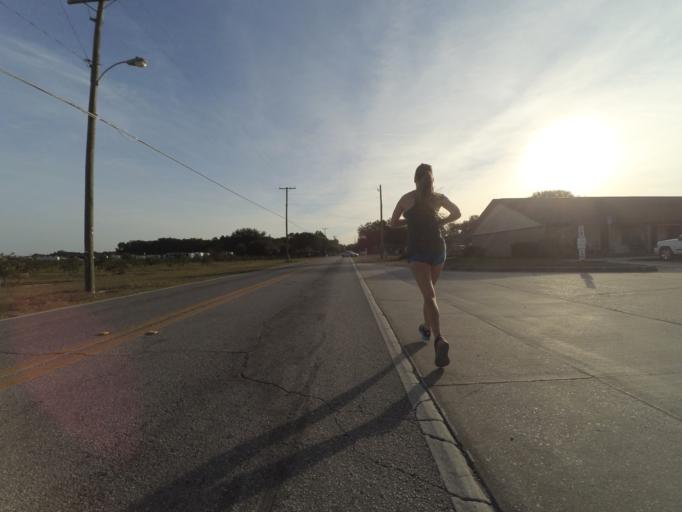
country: US
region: Florida
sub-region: Lake County
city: Umatilla
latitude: 28.9349
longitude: -81.6619
